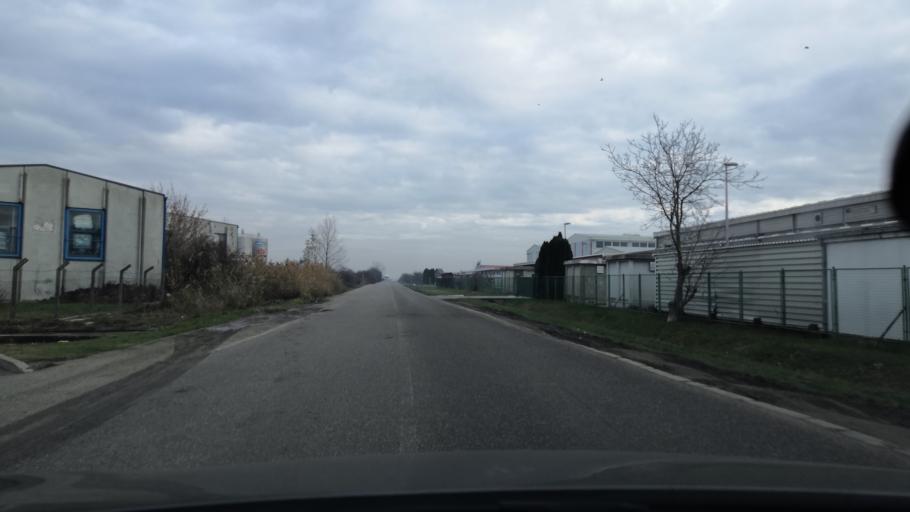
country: RS
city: Simanovci
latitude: 44.8785
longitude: 20.1300
